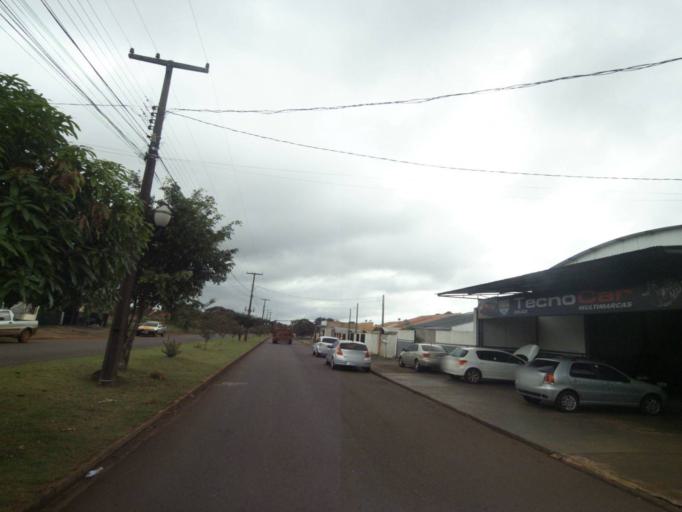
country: BR
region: Parana
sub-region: Campo Mourao
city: Campo Mourao
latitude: -24.0280
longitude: -52.3578
